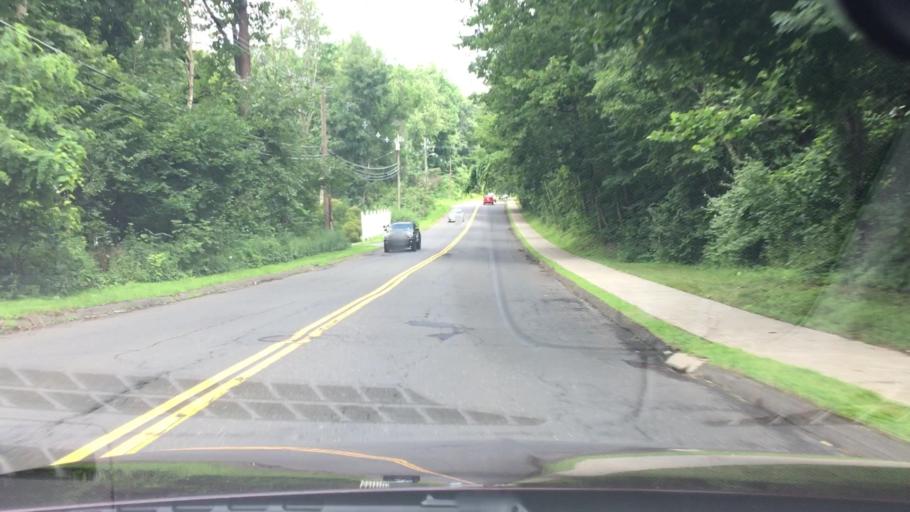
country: US
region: Connecticut
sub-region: Fairfield County
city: Danbury
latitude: 41.4287
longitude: -73.4231
